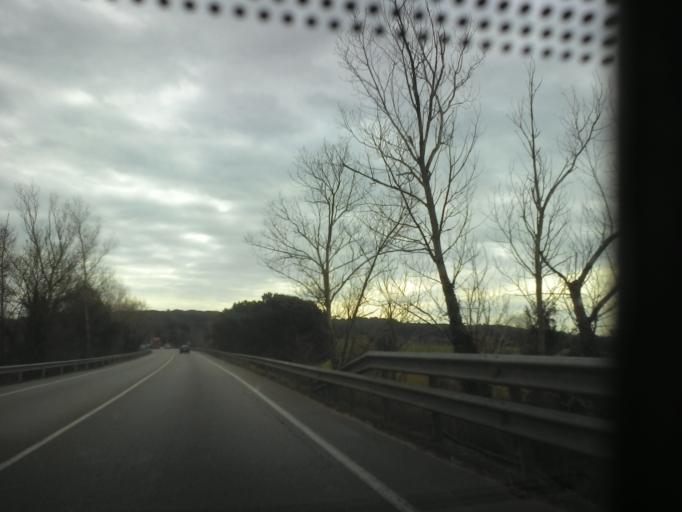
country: ES
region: Catalonia
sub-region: Provincia de Girona
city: Fornells de la Selva
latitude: 41.9390
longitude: 2.8212
